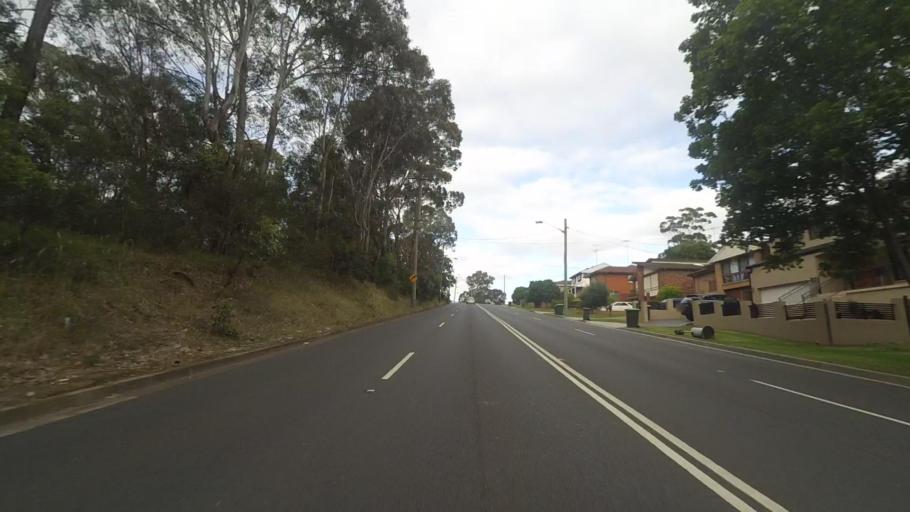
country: AU
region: New South Wales
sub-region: Bankstown
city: Bankstown
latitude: -33.9162
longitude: 151.0104
